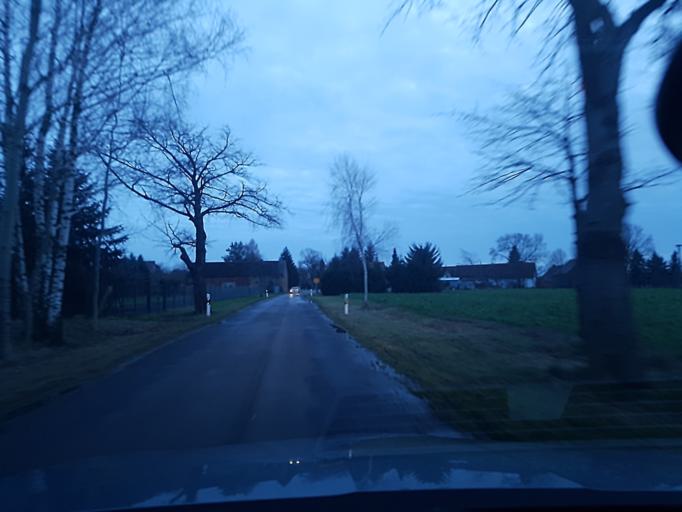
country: DE
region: Brandenburg
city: Finsterwalde
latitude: 51.6070
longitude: 13.6705
